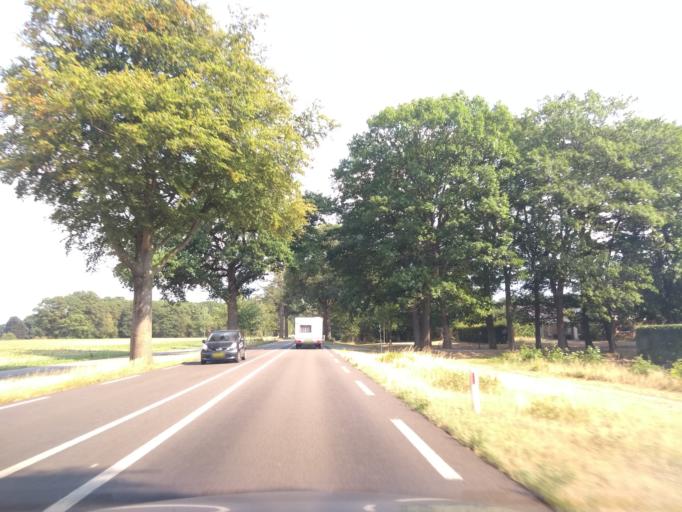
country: NL
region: Gelderland
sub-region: Gemeente Winterswijk
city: Winterswijk
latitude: 51.9923
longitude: 6.6833
